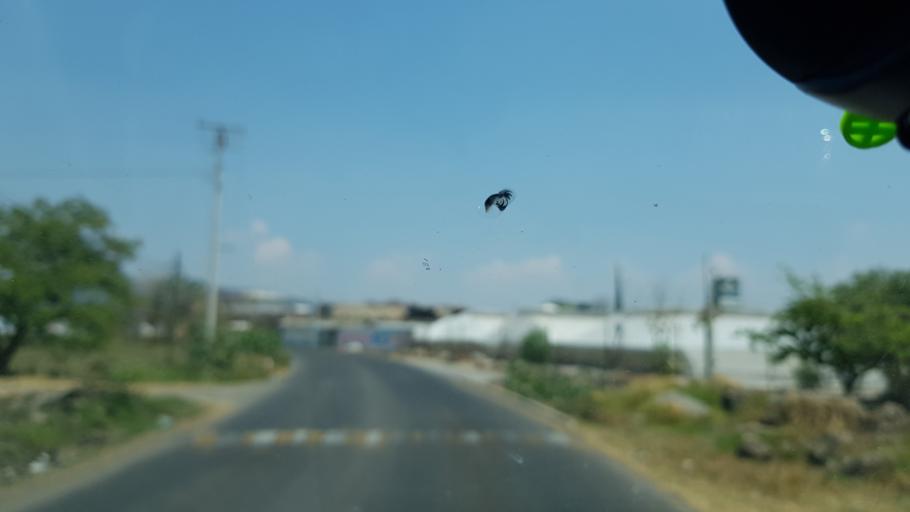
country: MX
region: Puebla
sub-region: Huaquechula
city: Cacaloxuchitl
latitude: 18.7889
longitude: -98.4727
